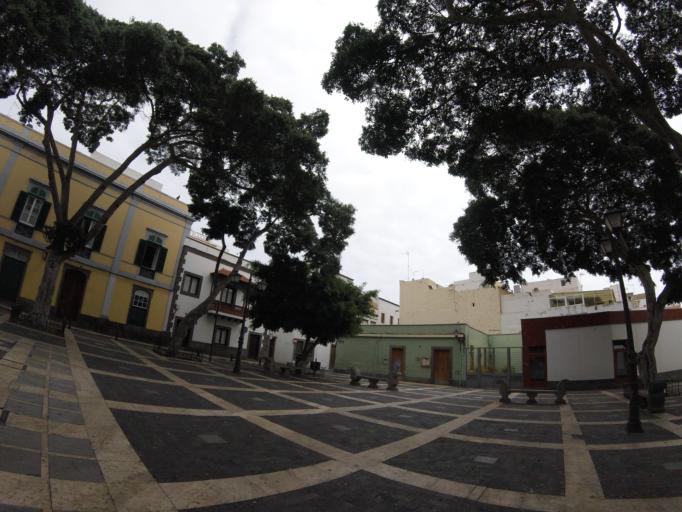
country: ES
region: Canary Islands
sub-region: Provincia de Las Palmas
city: Las Palmas de Gran Canaria
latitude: 28.0986
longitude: -15.4159
